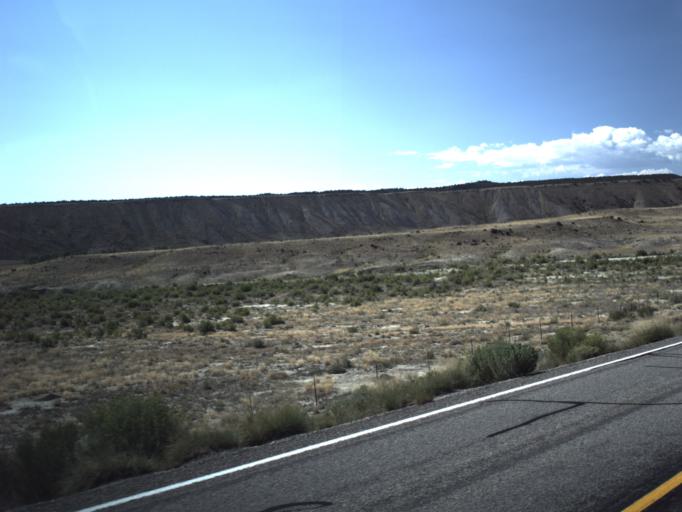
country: US
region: Utah
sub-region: Emery County
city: Ferron
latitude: 38.8058
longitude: -111.3381
